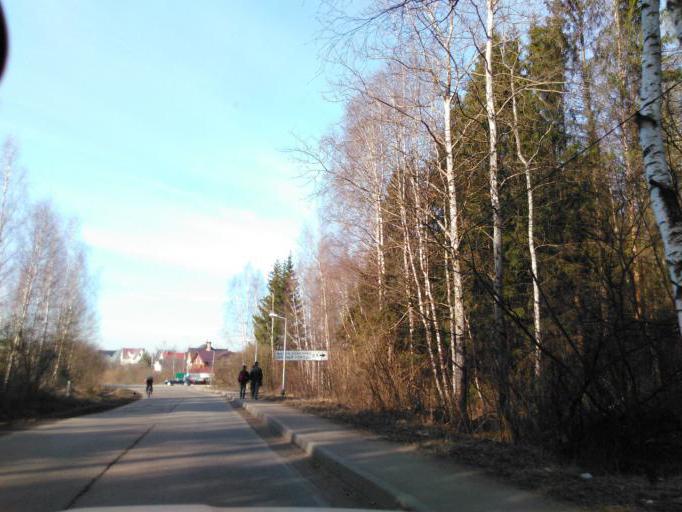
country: RU
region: Moskovskaya
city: Firsanovka
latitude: 55.9157
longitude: 37.2000
